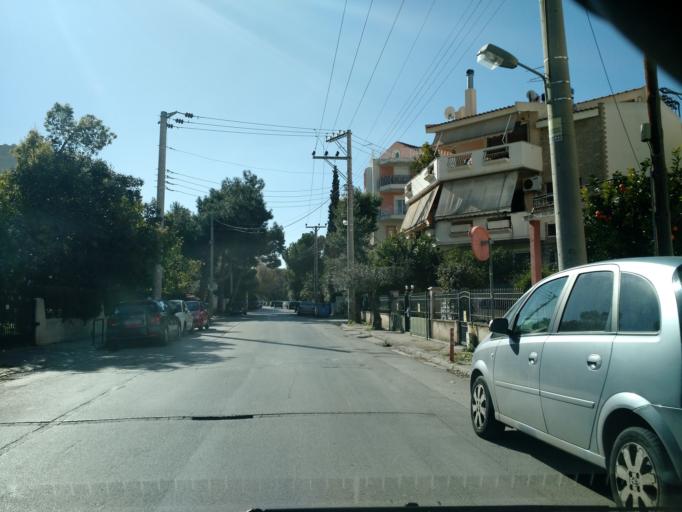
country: GR
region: Attica
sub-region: Nomarchia Athinas
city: Agia Paraskevi
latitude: 38.0195
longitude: 23.8190
